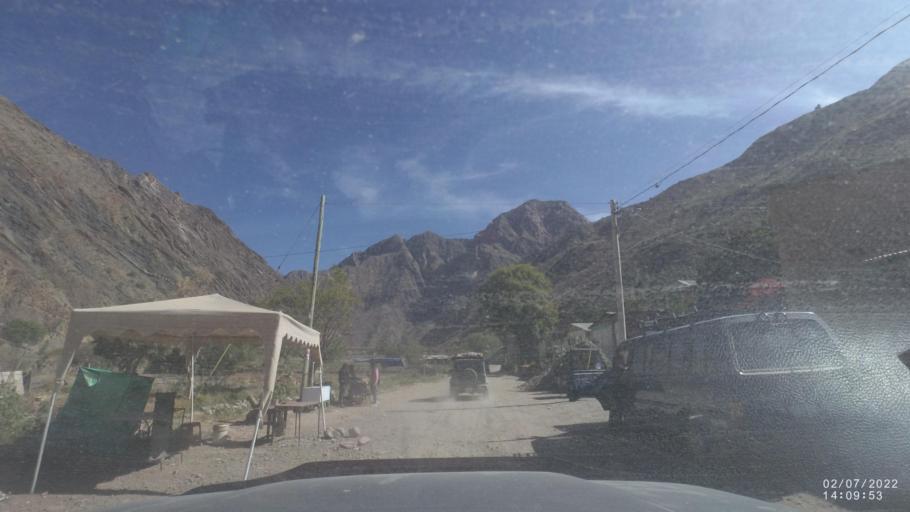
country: BO
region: Cochabamba
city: Irpa Irpa
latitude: -17.8228
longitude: -66.4031
